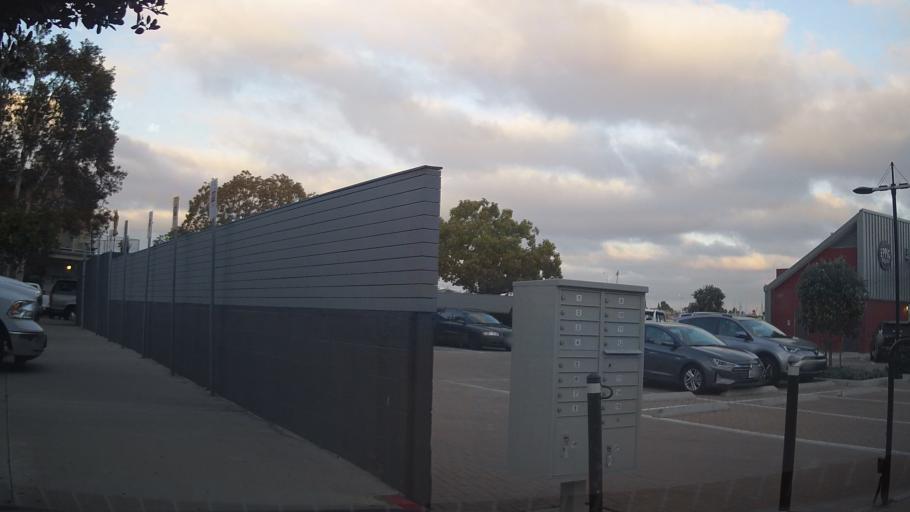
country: US
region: California
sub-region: San Diego County
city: Coronado
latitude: 32.7227
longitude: -117.2281
